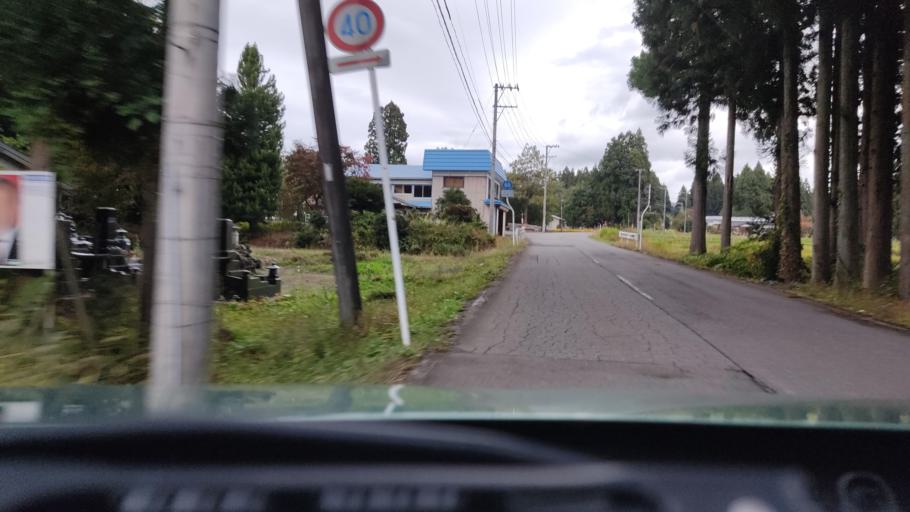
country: JP
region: Akita
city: Kakunodatemachi
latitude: 39.5713
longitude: 140.6130
